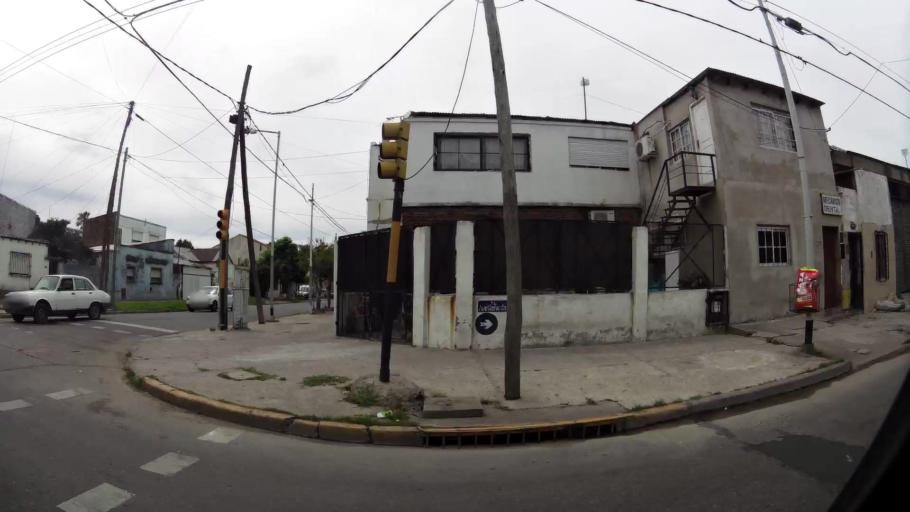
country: AR
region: Buenos Aires
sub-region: Partido de Avellaneda
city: Avellaneda
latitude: -34.6578
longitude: -58.3480
